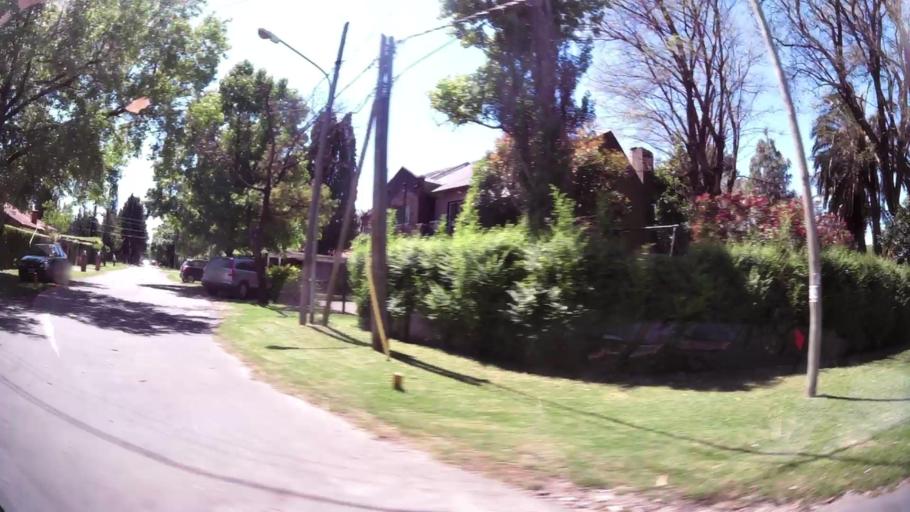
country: AR
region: Buenos Aires
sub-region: Partido de Tigre
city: Tigre
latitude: -34.4927
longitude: -58.6427
